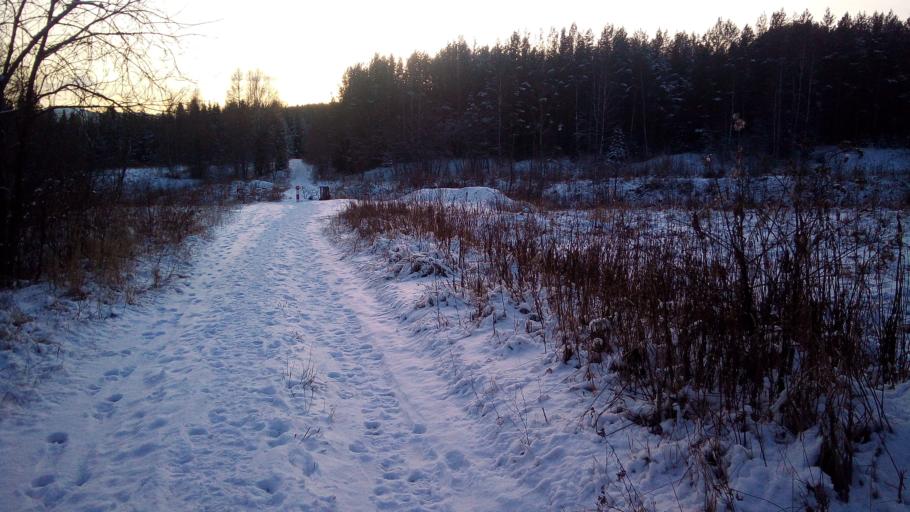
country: RU
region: Chelyabinsk
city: Bakal
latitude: 54.8150
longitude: 59.0011
